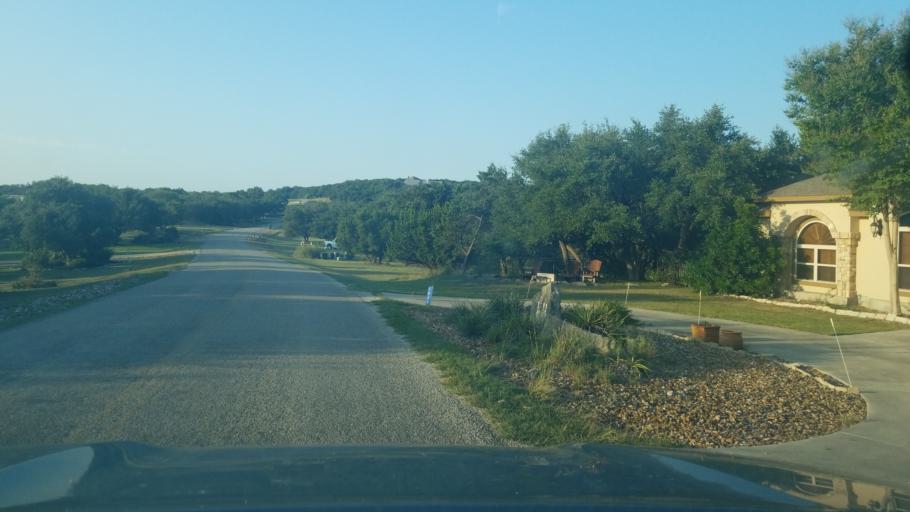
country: US
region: Texas
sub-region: Comal County
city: Bulverde
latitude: 29.8242
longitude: -98.4073
